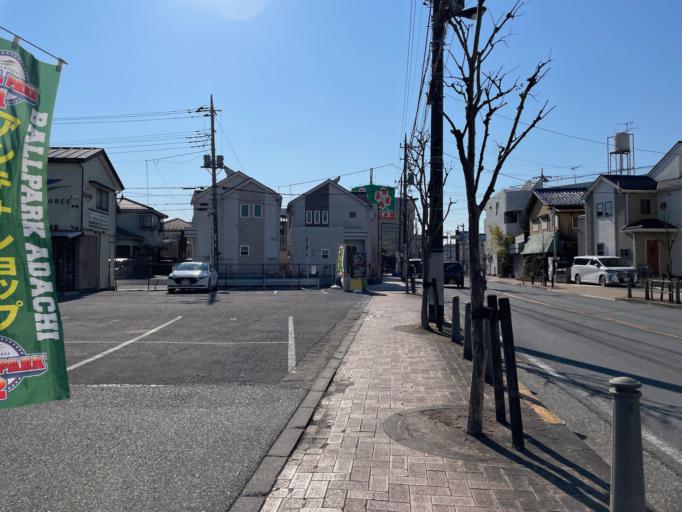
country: JP
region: Saitama
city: Soka
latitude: 35.8028
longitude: 139.7833
